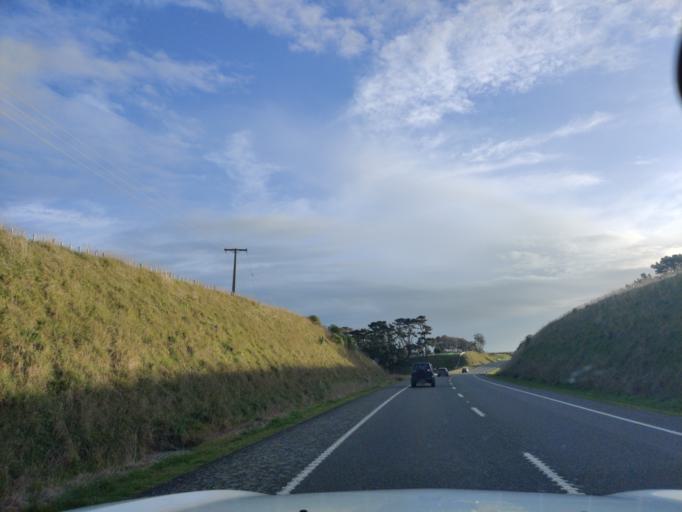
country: NZ
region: Manawatu-Wanganui
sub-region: Horowhenua District
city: Foxton
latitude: -40.5123
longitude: 175.4652
